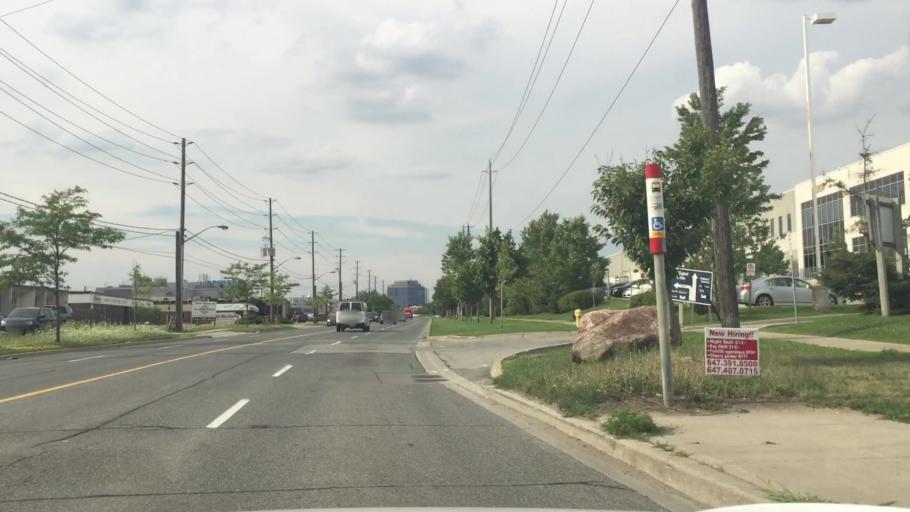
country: CA
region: Ontario
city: Concord
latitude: 43.7599
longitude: -79.5394
